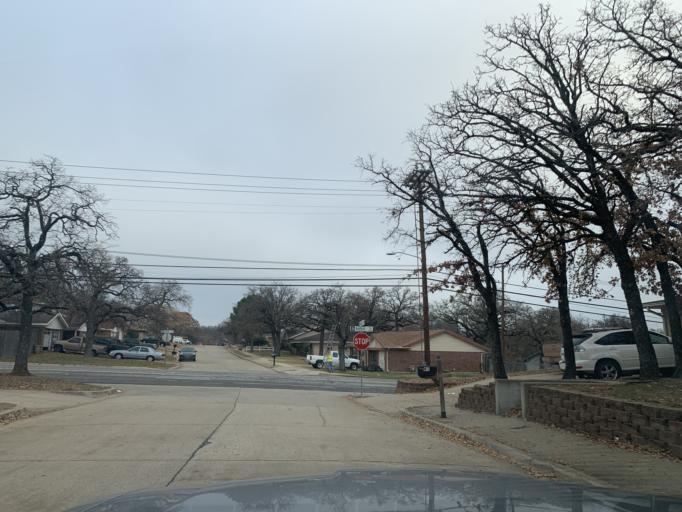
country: US
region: Texas
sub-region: Tarrant County
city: Bedford
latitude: 32.8361
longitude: -97.1555
